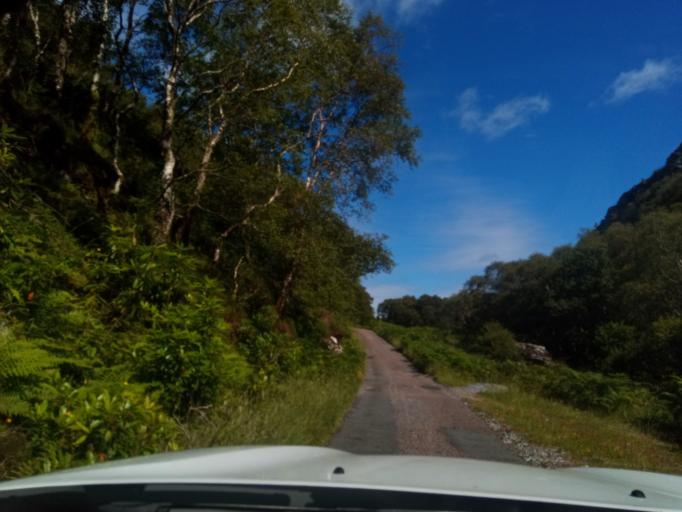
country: GB
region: Scotland
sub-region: Argyll and Bute
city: Isle Of Mull
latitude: 56.7694
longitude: -5.8234
